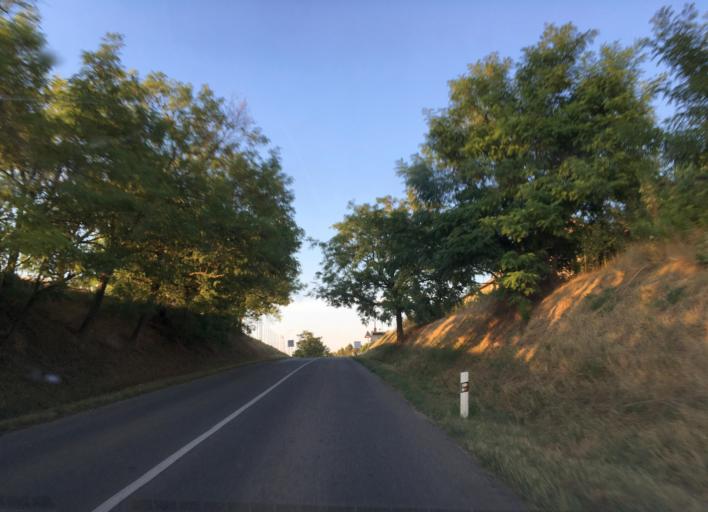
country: HU
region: Komarom-Esztergom
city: Neszmely
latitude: 47.8164
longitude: 18.3491
